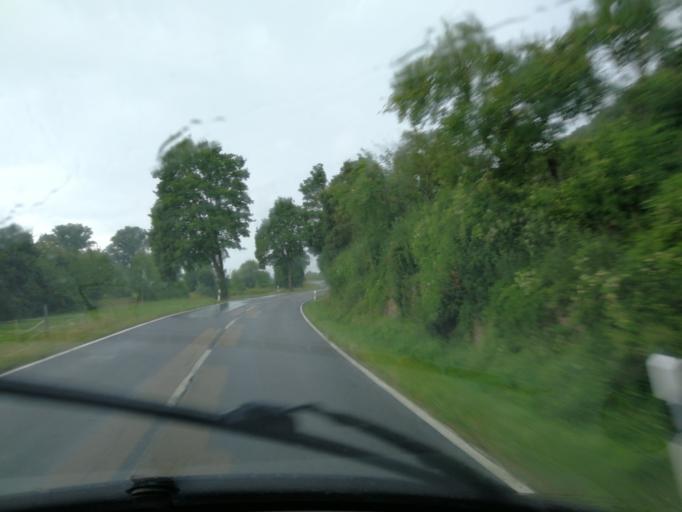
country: DE
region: Bavaria
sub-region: Upper Palatinate
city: Donaustauf
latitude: 49.0226
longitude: 12.2747
